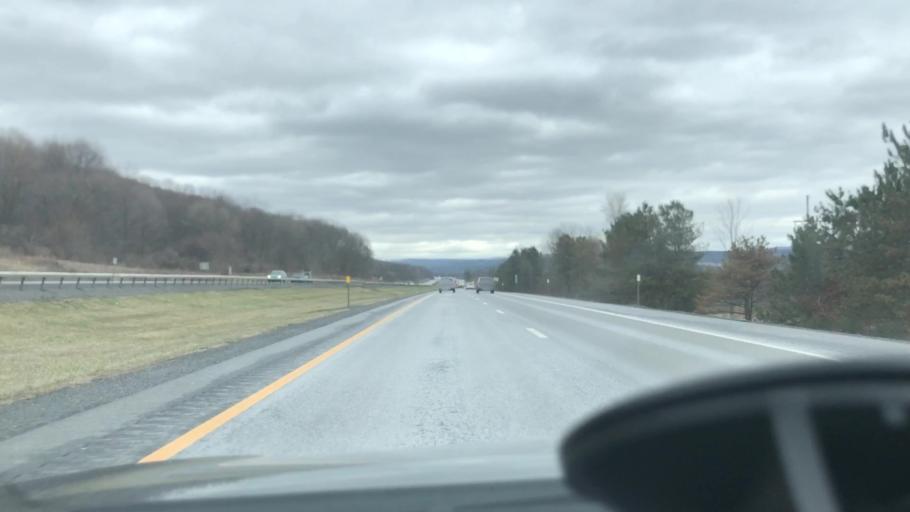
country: US
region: New York
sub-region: Herkimer County
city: Frankfort
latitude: 43.0479
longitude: -75.0591
